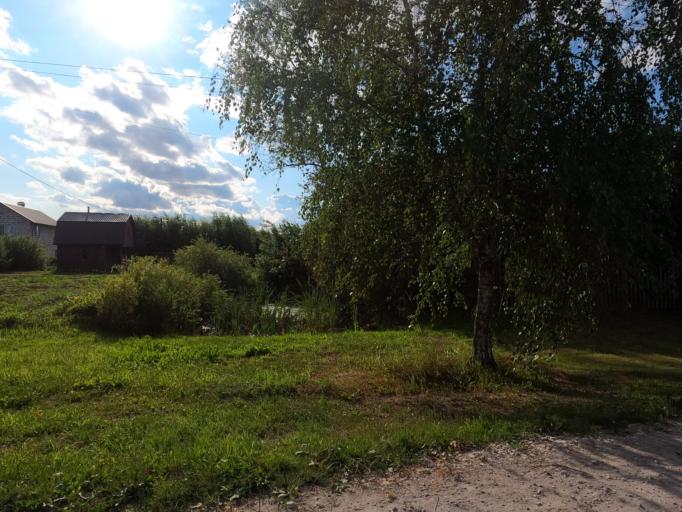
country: RU
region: Moskovskaya
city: Konobeyevo
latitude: 55.4095
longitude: 38.7180
